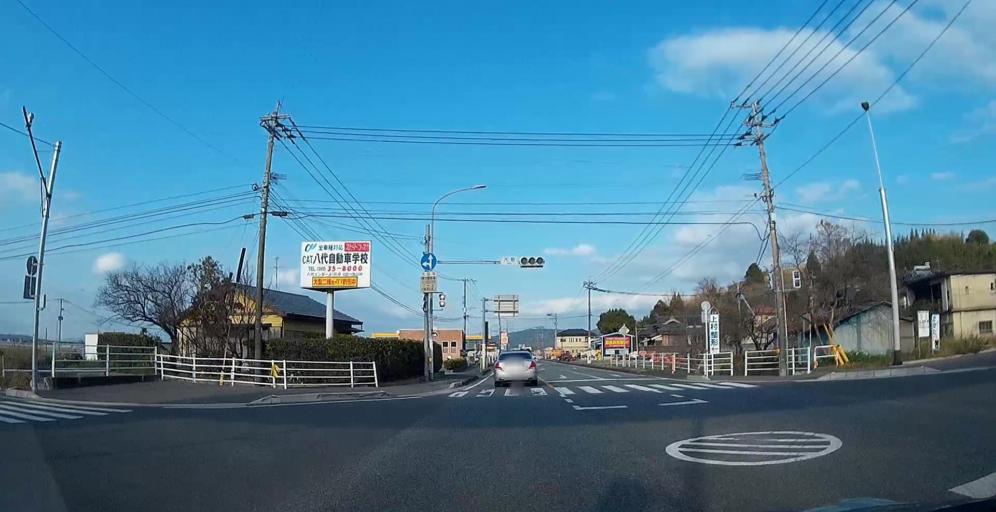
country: JP
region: Kumamoto
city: Matsubase
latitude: 32.5778
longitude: 130.6959
